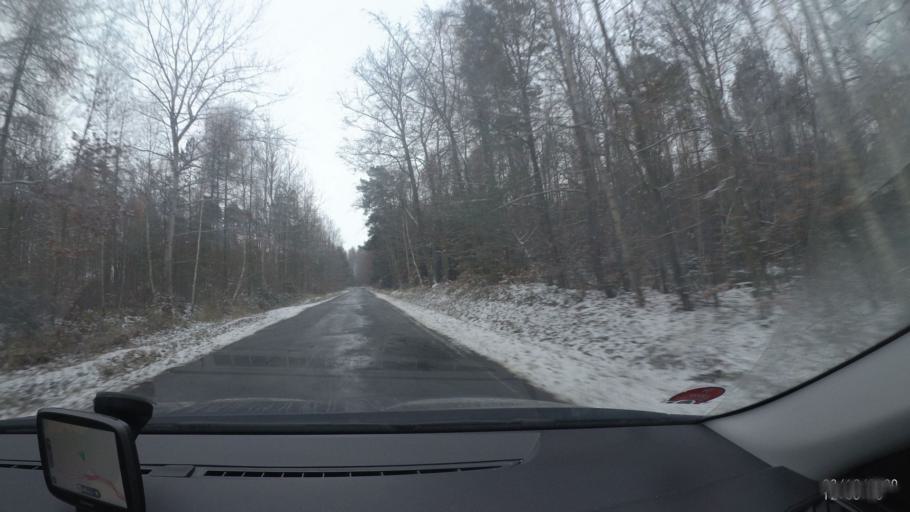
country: CZ
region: Central Bohemia
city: Nove Straseci
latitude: 50.1697
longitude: 13.8674
